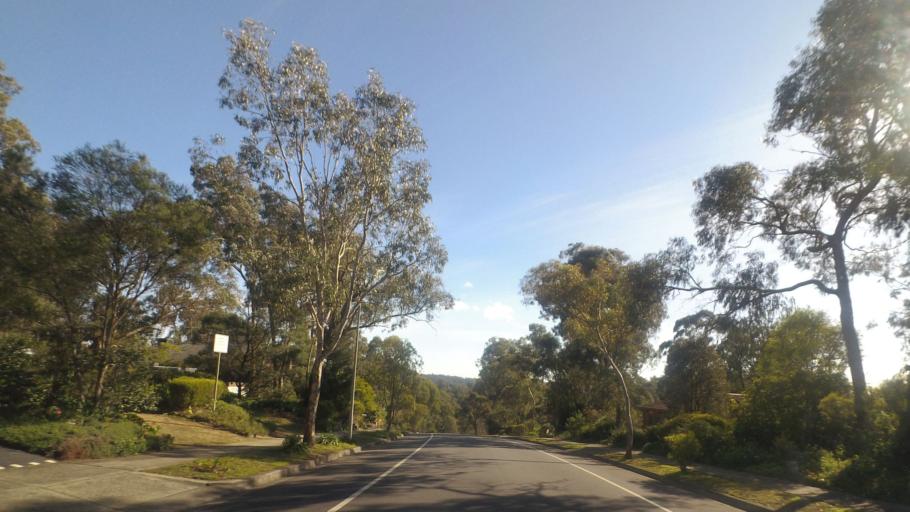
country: AU
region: Victoria
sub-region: Nillumbik
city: Eltham North
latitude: -37.7123
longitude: 145.1606
